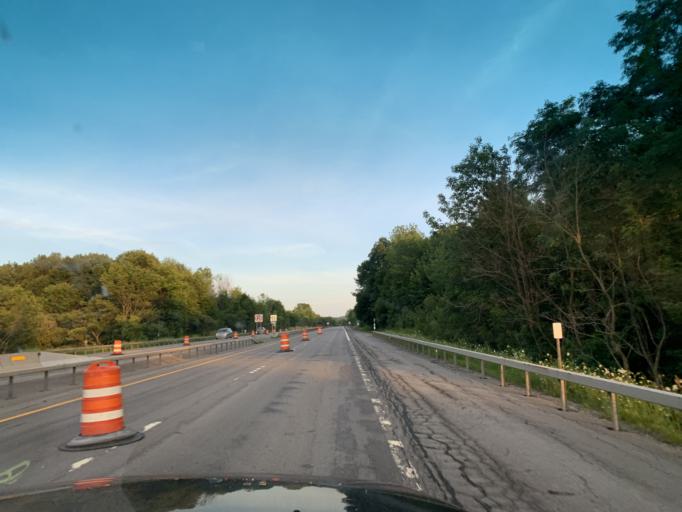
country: US
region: New York
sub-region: Oneida County
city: Chadwicks
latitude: 43.0216
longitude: -75.2603
